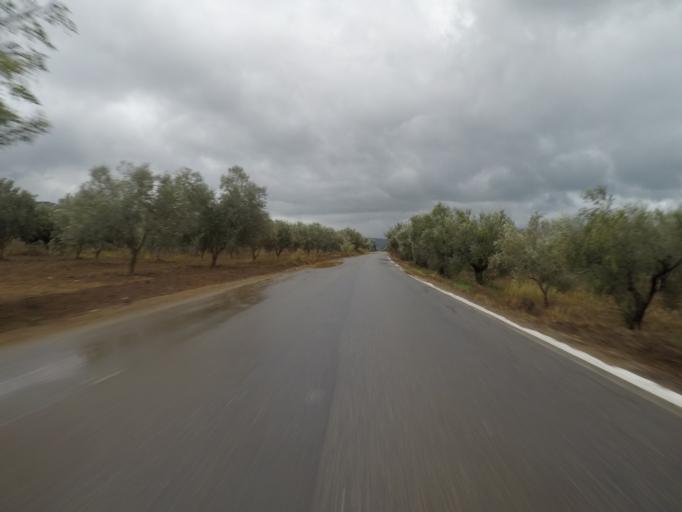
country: GR
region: Peloponnese
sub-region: Nomos Messinias
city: Pylos
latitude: 36.9745
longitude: 21.6879
